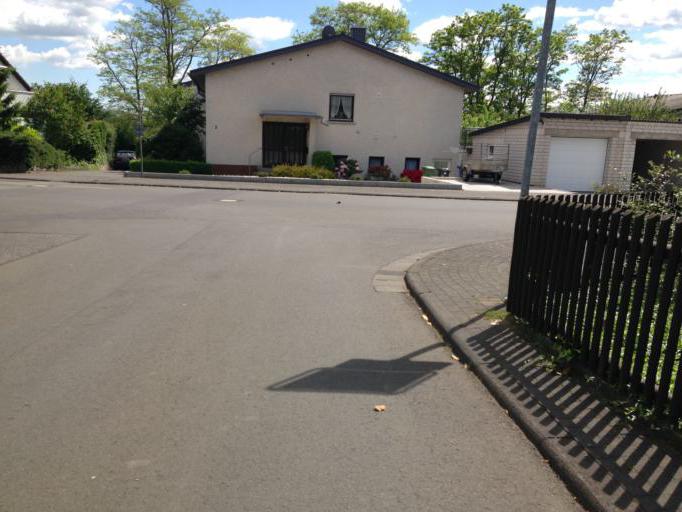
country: DE
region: Hesse
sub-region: Regierungsbezirk Giessen
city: Heuchelheim
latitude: 50.5862
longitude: 8.6117
